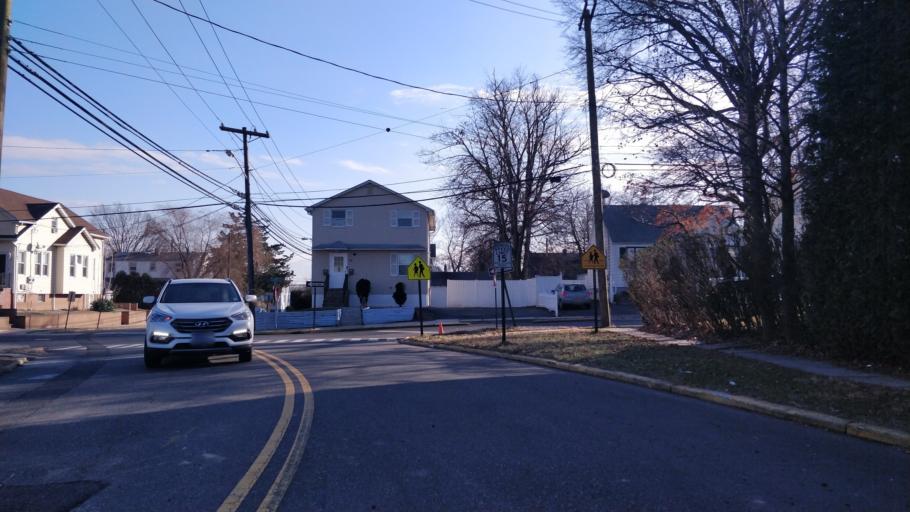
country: US
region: New Jersey
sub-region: Union County
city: Hillside
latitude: 40.7006
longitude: -74.2437
